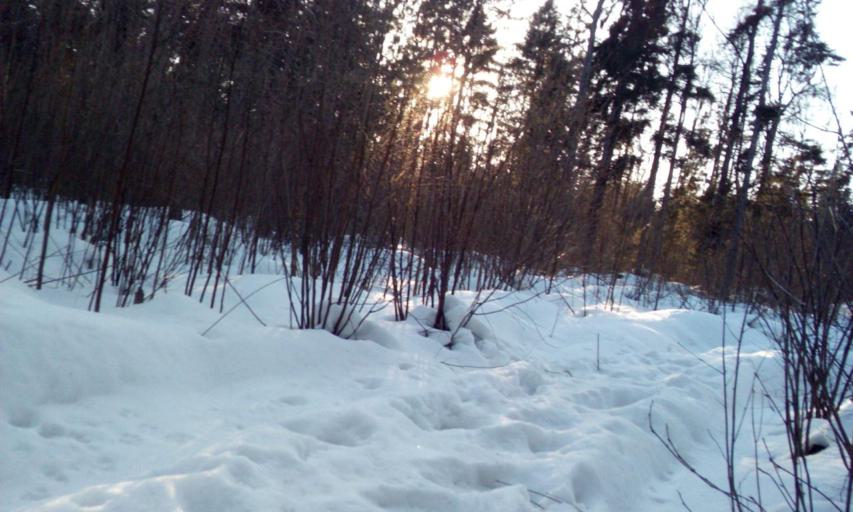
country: RU
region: Moscow
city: Tolstopal'tsevo
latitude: 55.6224
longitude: 37.2431
